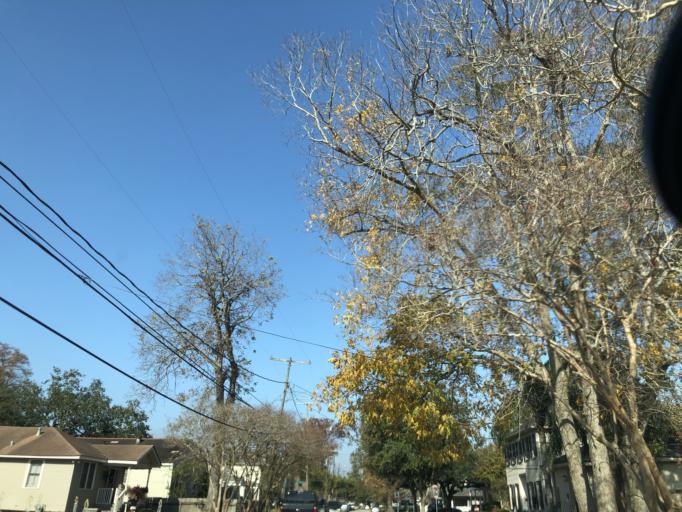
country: US
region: Louisiana
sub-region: Jefferson Parish
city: Metairie
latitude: 29.9852
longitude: -90.1527
